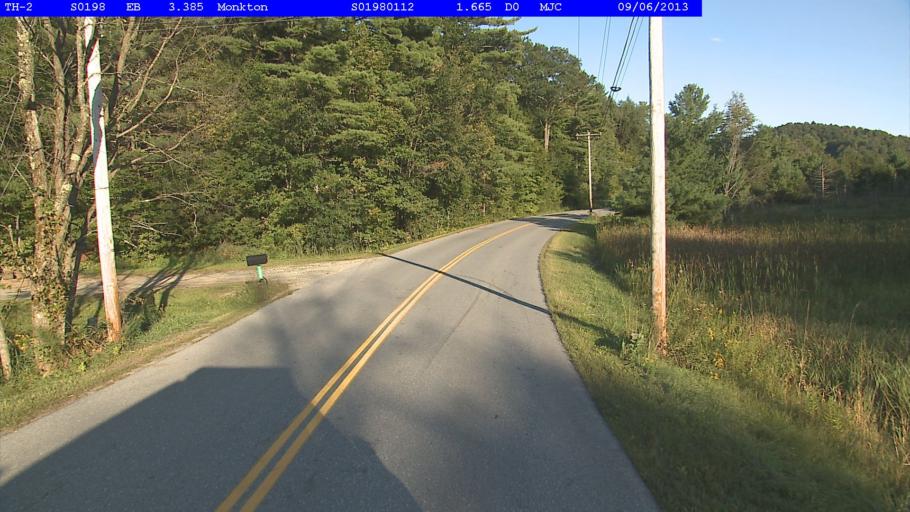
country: US
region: Vermont
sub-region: Chittenden County
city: Hinesburg
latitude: 44.2460
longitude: -73.1671
